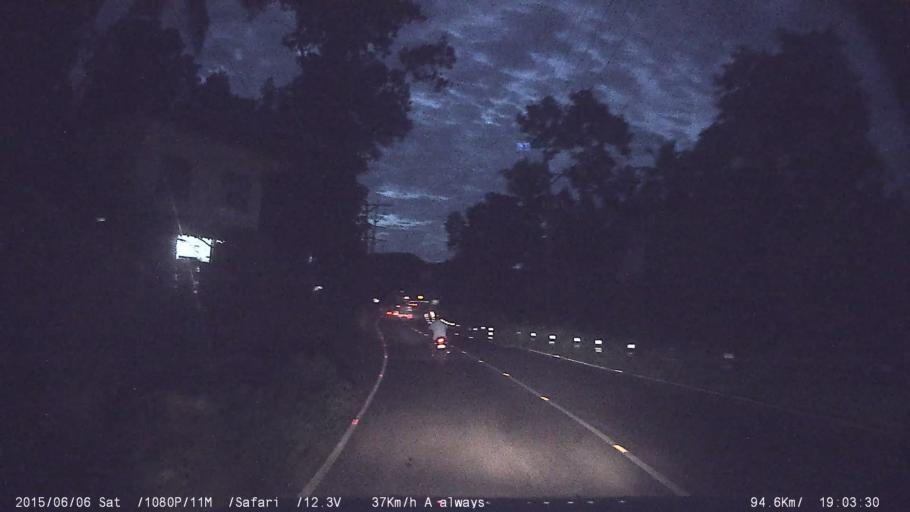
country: IN
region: Kerala
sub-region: Kottayam
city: Changanacheri
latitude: 9.4827
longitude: 76.5738
